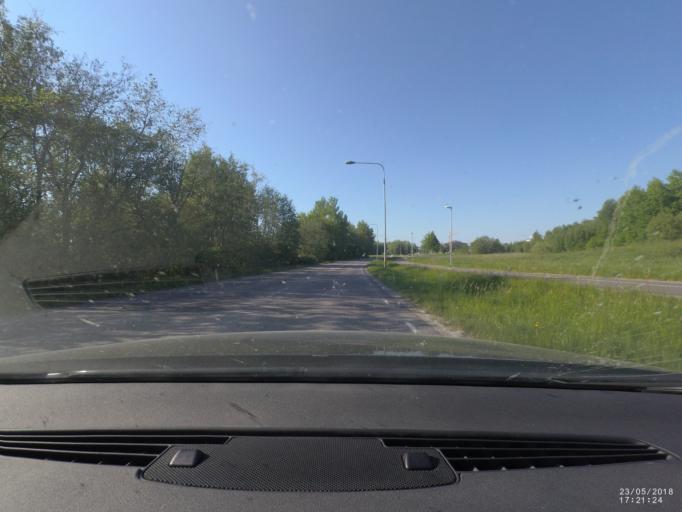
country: SE
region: Soedermanland
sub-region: Nykopings Kommun
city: Nykoping
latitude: 58.7356
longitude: 17.0055
